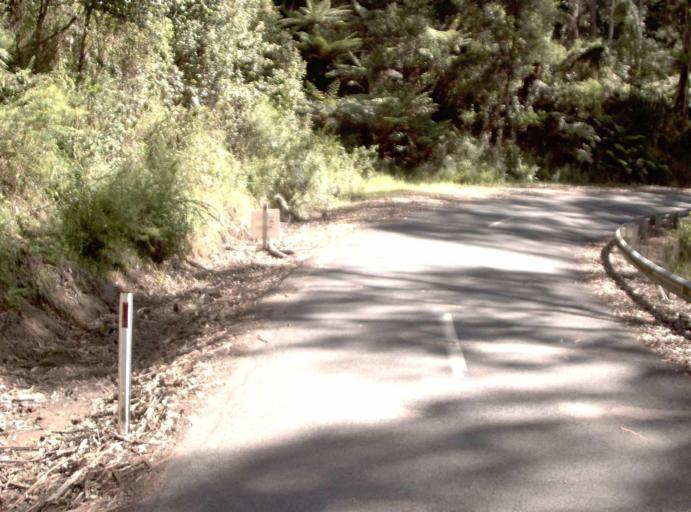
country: AU
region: New South Wales
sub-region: Bombala
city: Bombala
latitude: -37.3797
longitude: 148.6262
